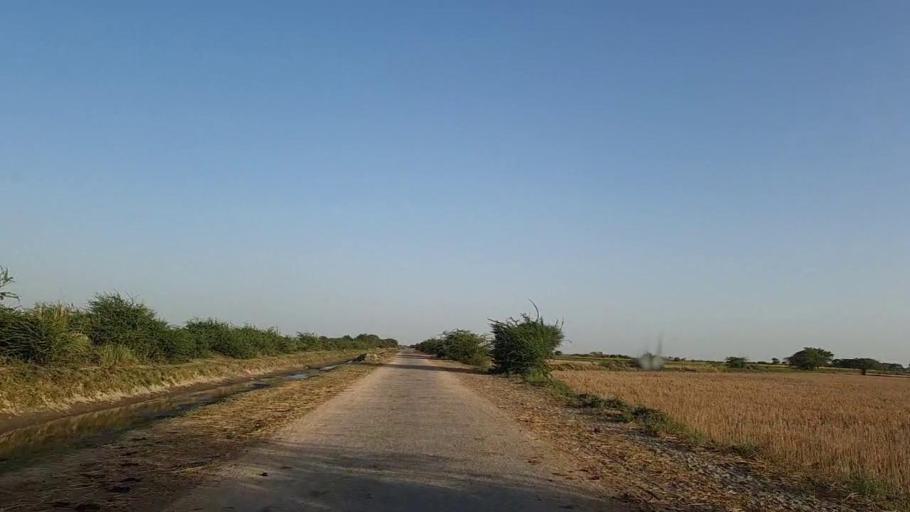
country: PK
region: Sindh
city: Jati
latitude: 24.4103
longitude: 68.3488
